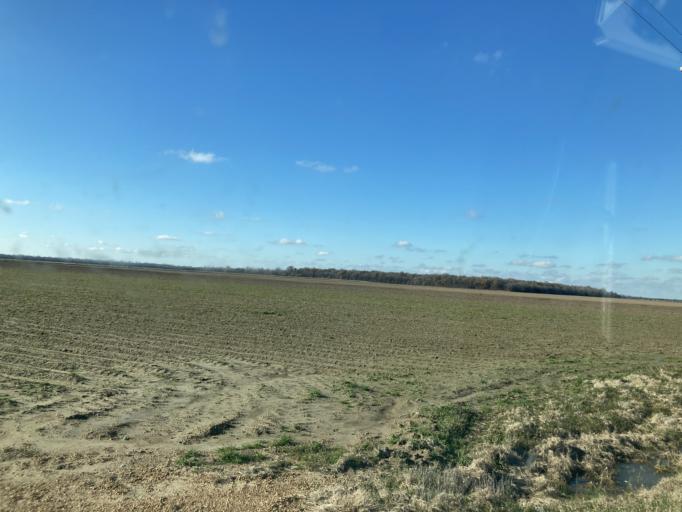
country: US
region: Mississippi
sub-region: Yazoo County
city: Yazoo City
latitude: 32.9297
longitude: -90.5058
